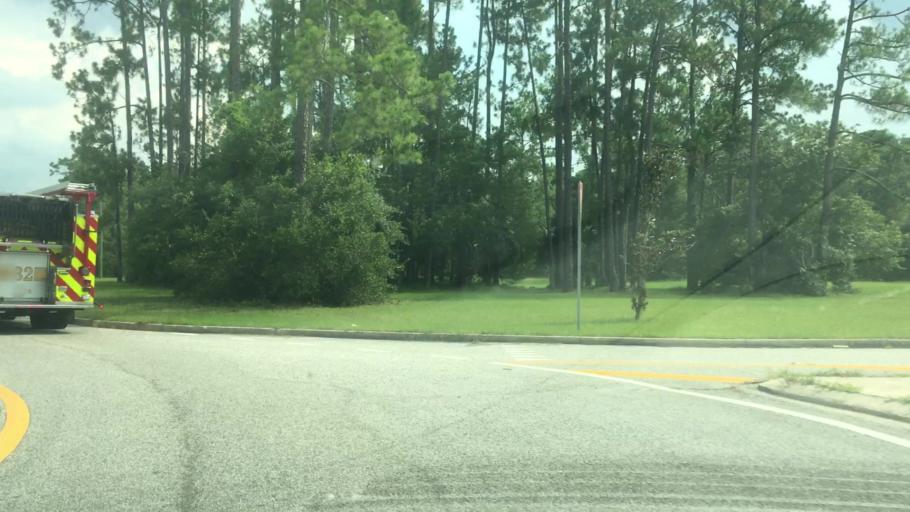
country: US
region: Florida
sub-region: Duval County
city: Neptune Beach
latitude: 30.2908
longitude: -81.5051
